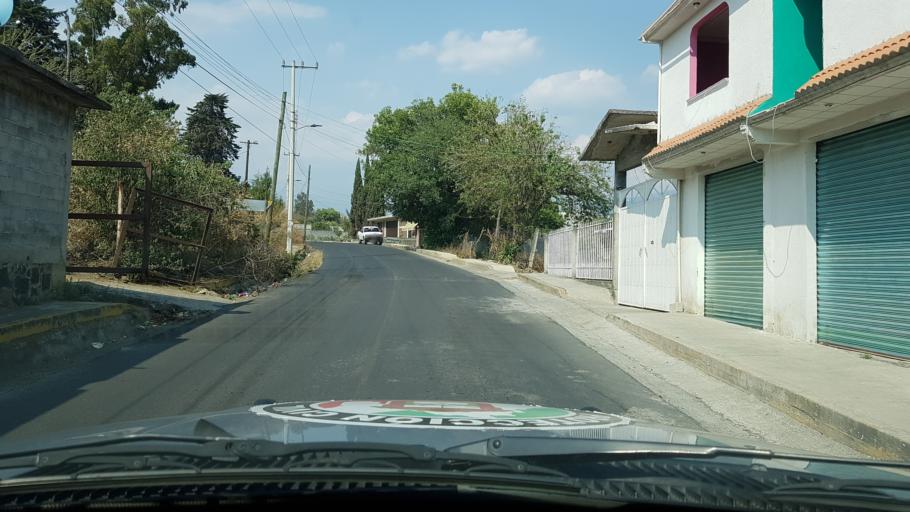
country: MX
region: Mexico
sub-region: Ozumba
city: San Jose Tlacotitlan
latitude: 18.9782
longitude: -98.8121
